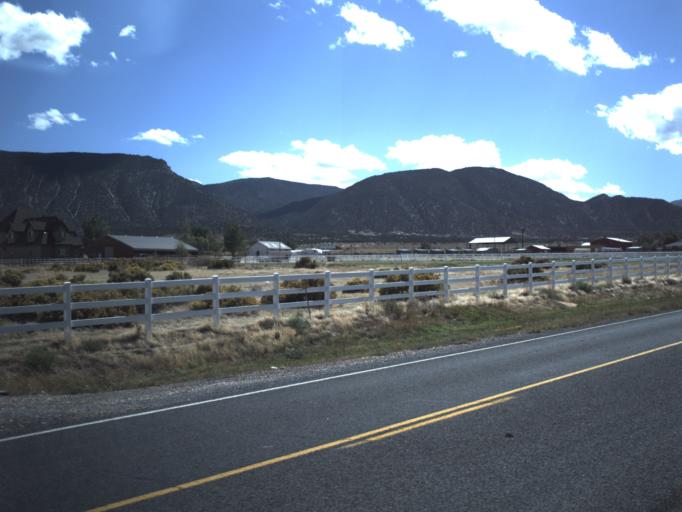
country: US
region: Utah
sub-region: Iron County
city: Enoch
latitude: 37.7385
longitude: -113.0553
